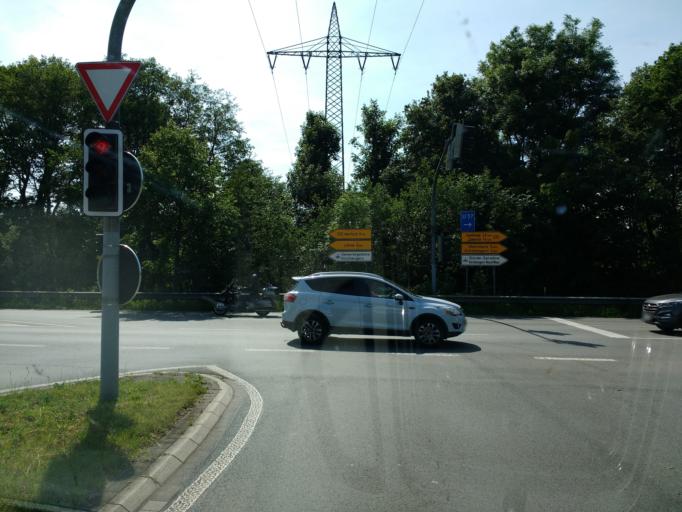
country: DE
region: North Rhine-Westphalia
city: Loehne
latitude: 52.1877
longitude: 8.6623
